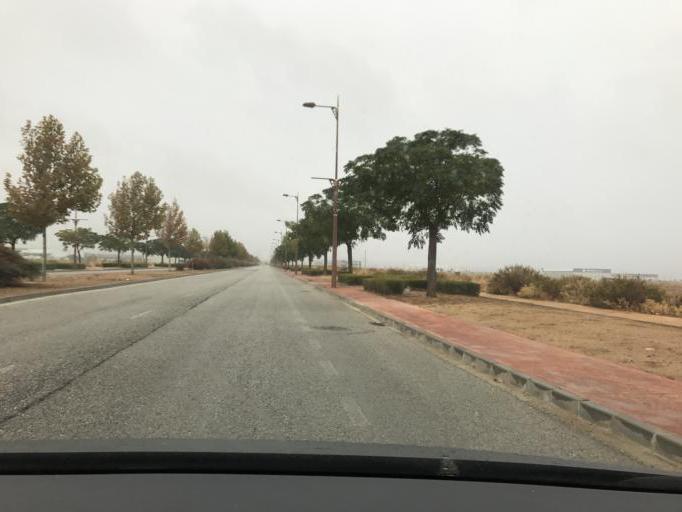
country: ES
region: Andalusia
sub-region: Provincia de Granada
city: Escuzar
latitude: 37.0839
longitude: -3.7684
